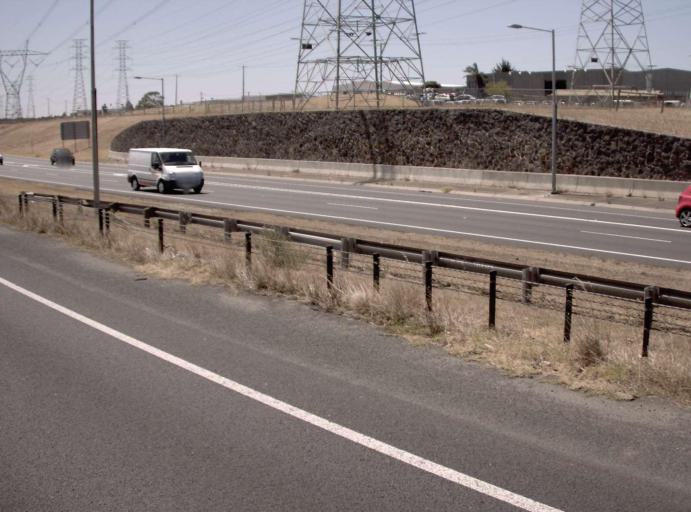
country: AU
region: Victoria
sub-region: Moonee Valley
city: Keilor East
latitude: -37.7322
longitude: 144.8542
